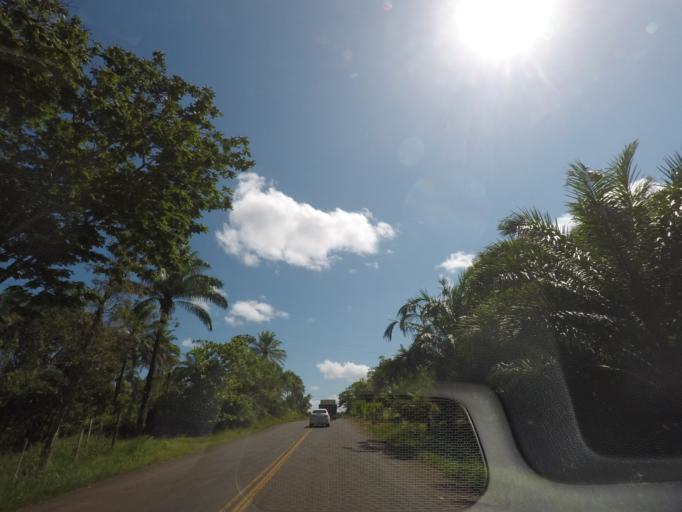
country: BR
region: Bahia
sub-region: Itubera
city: Itubera
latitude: -13.6670
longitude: -39.1204
